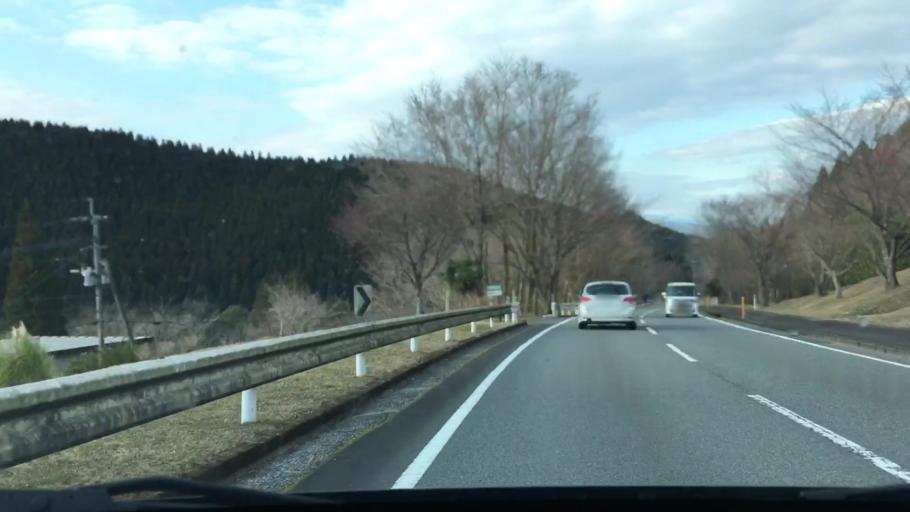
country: JP
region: Miyazaki
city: Miyazaki-shi
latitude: 31.8024
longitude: 131.3018
